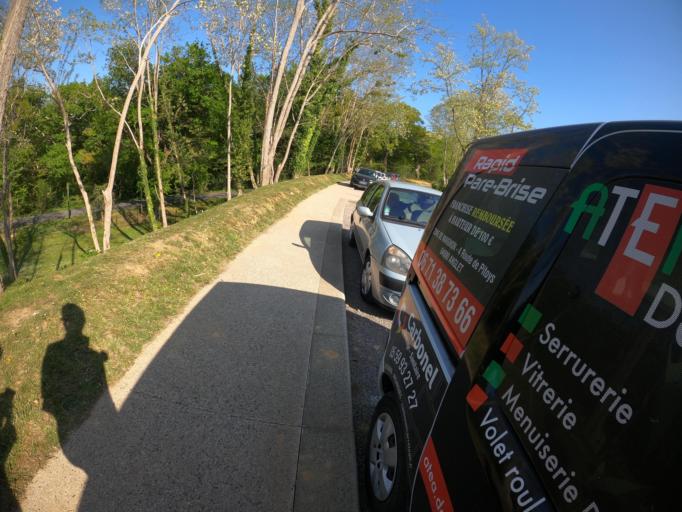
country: FR
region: Aquitaine
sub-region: Departement des Pyrenees-Atlantiques
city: Arcangues
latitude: 43.4369
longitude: -1.5206
